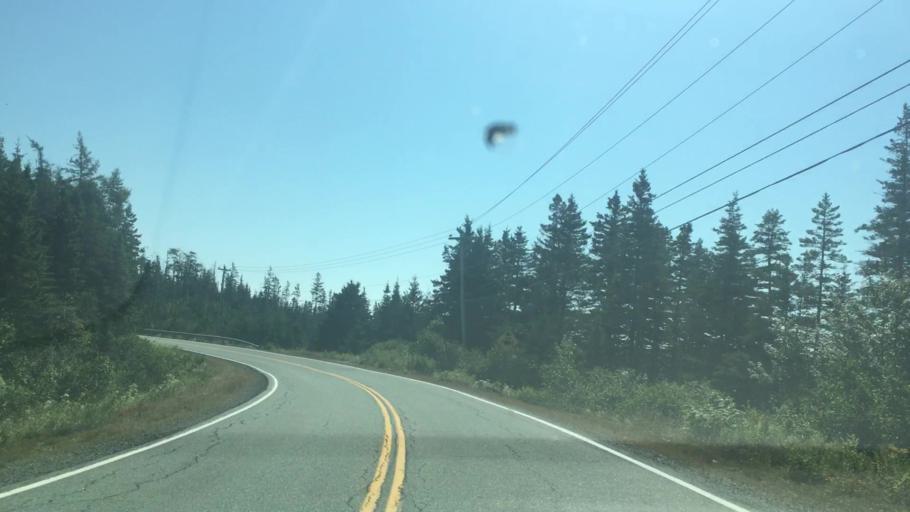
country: CA
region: Nova Scotia
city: Antigonish
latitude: 45.0078
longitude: -62.0899
